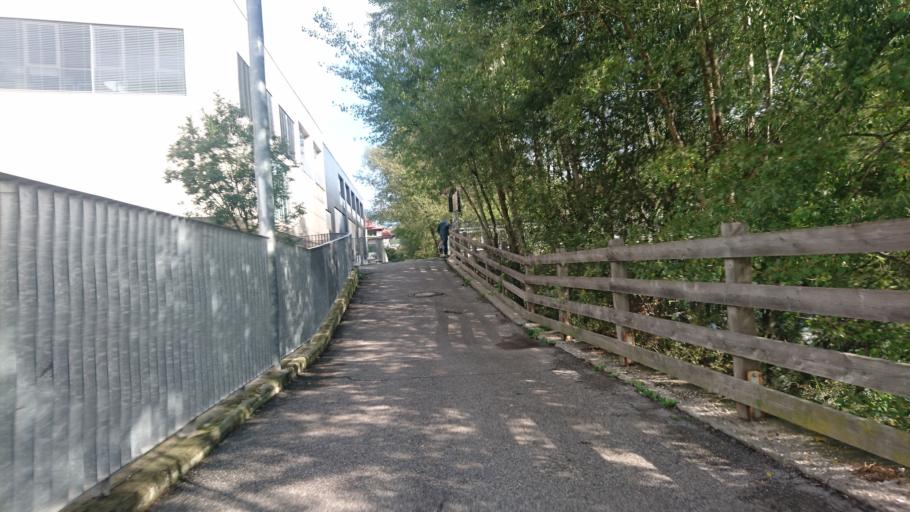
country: IT
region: Trentino-Alto Adige
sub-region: Bolzano
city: Leone-Santa Elisabetta
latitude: 46.7298
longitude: 11.6532
